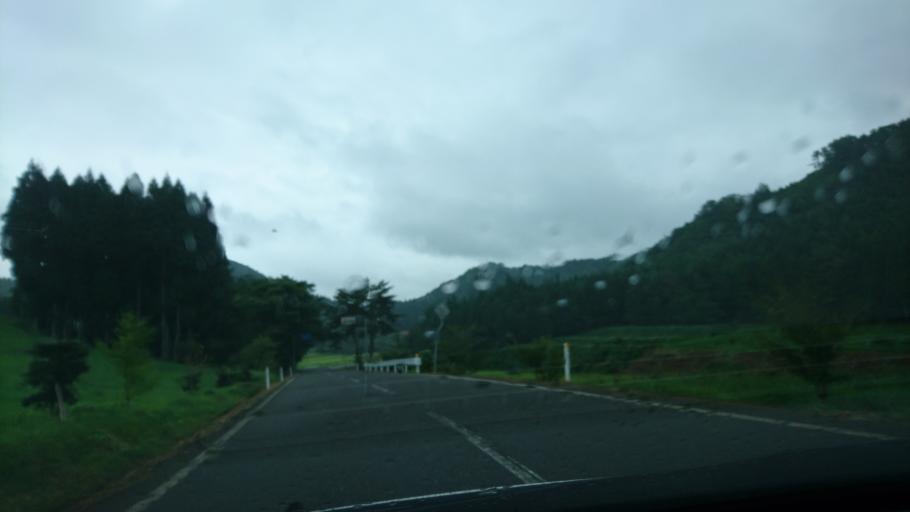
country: JP
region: Iwate
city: Ichinoseki
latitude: 38.8853
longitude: 140.9780
